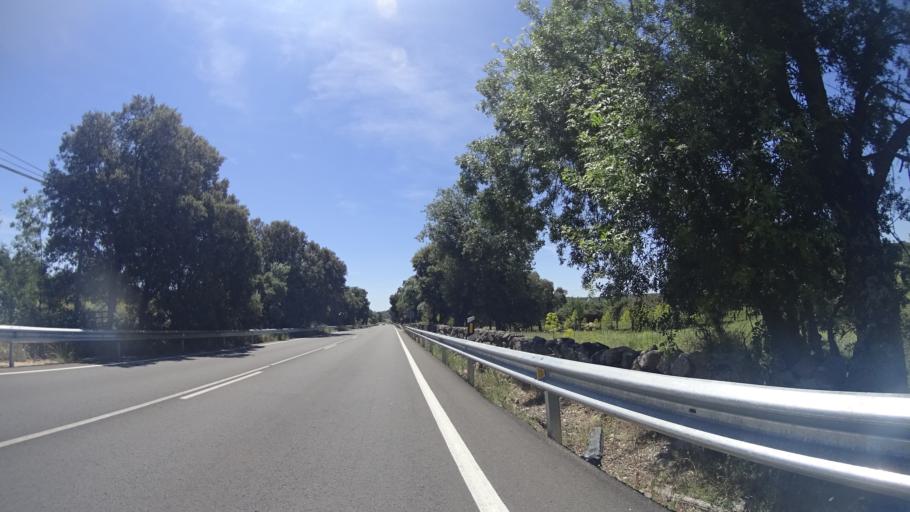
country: ES
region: Madrid
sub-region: Provincia de Madrid
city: Navalquejigo
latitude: 40.6032
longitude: -4.0209
